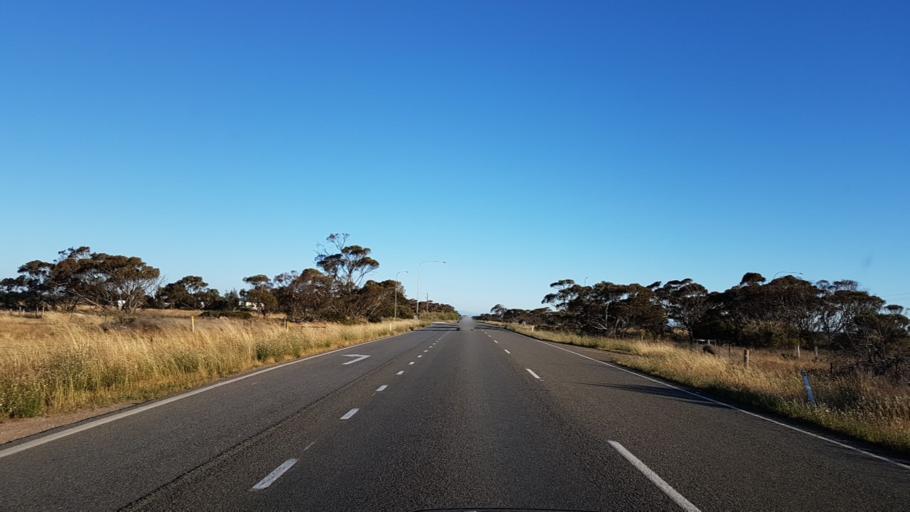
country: AU
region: South Australia
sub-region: Mallala
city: Mallala
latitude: -34.4755
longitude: 138.3791
